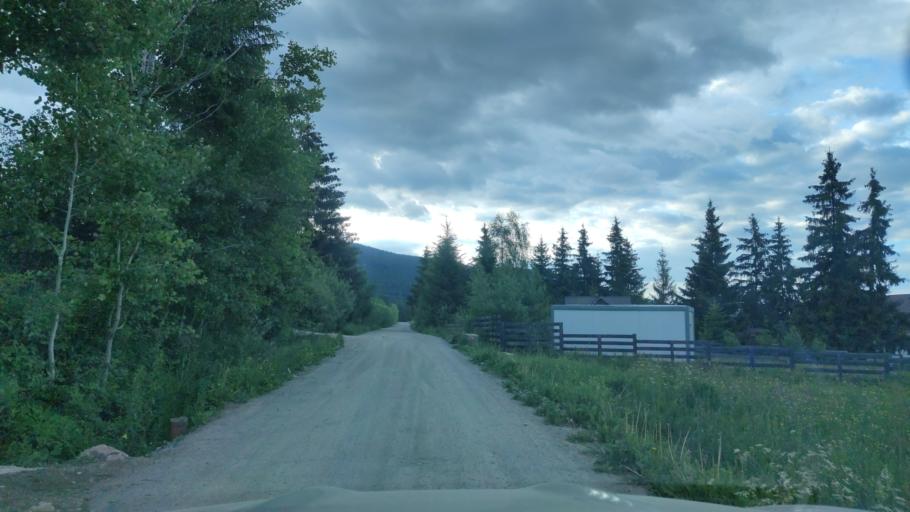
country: RO
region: Harghita
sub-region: Comuna Joseni
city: Joseni
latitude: 46.6694
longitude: 25.3732
